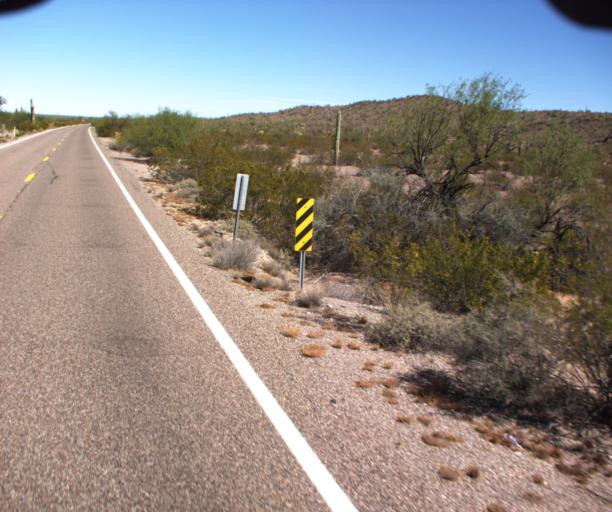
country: MX
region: Sonora
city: Sonoyta
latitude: 32.0011
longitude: -112.8062
